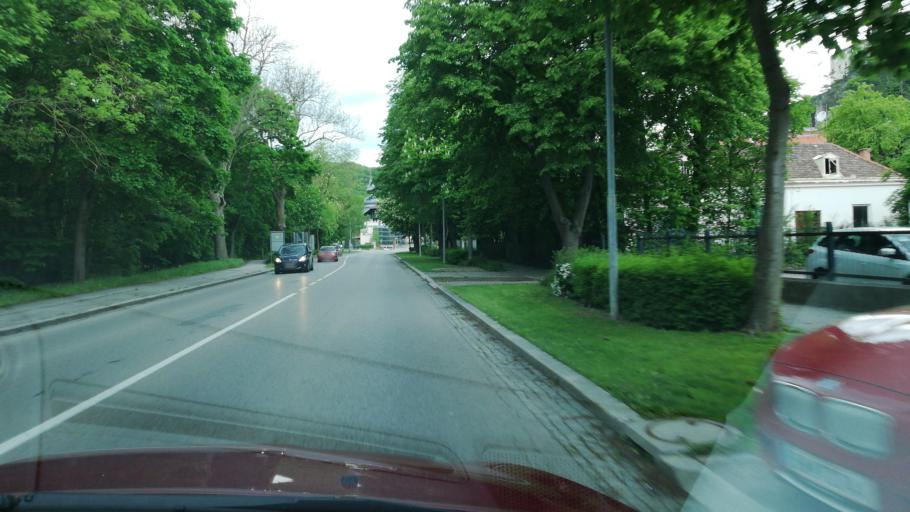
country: AT
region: Lower Austria
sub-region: Politischer Bezirk Baden
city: Baden
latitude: 48.0102
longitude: 16.2072
